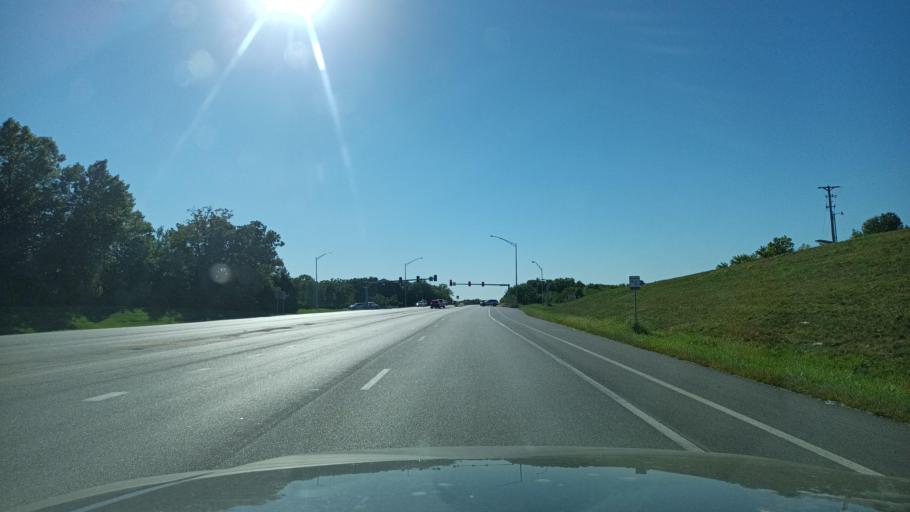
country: US
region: Missouri
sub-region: Boone County
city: Columbia
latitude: 38.9320
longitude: -92.2965
